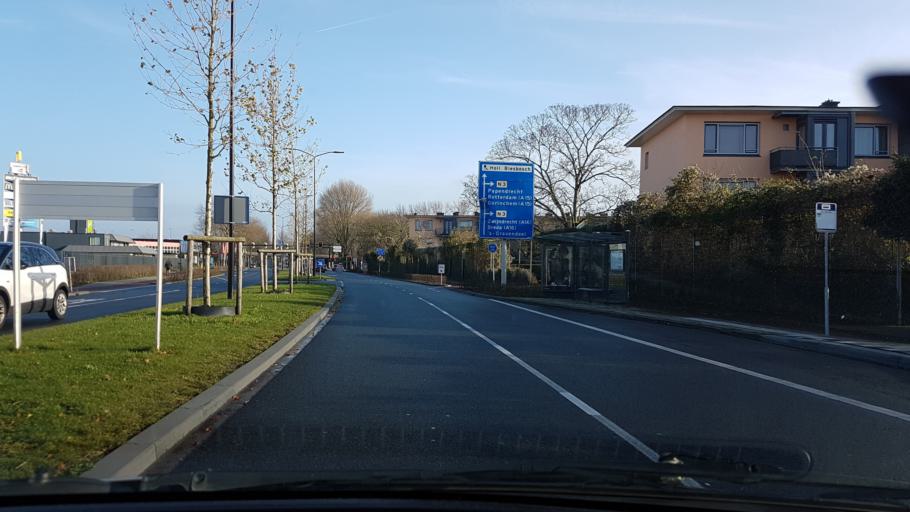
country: NL
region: South Holland
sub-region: Gemeente Papendrecht
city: Papendrecht
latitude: 51.8171
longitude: 4.7026
